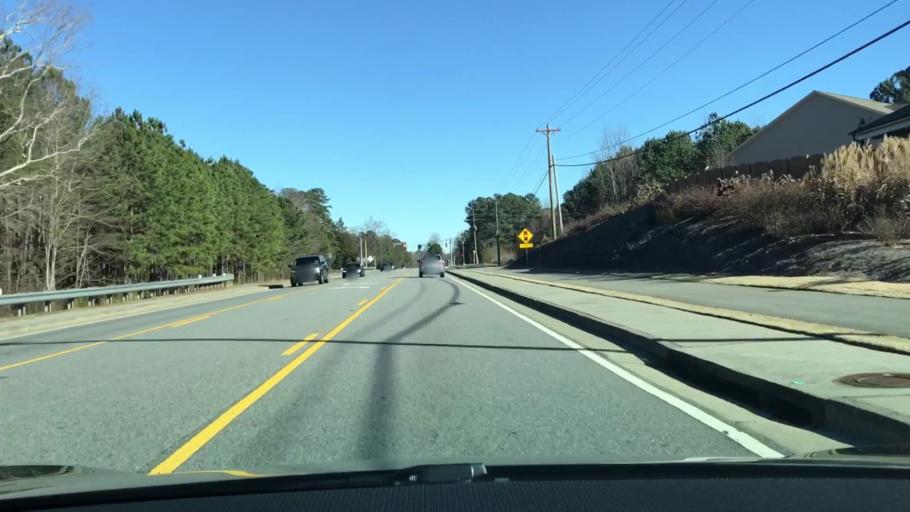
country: US
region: Georgia
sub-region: Forsyth County
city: Cumming
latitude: 34.1871
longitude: -84.1242
